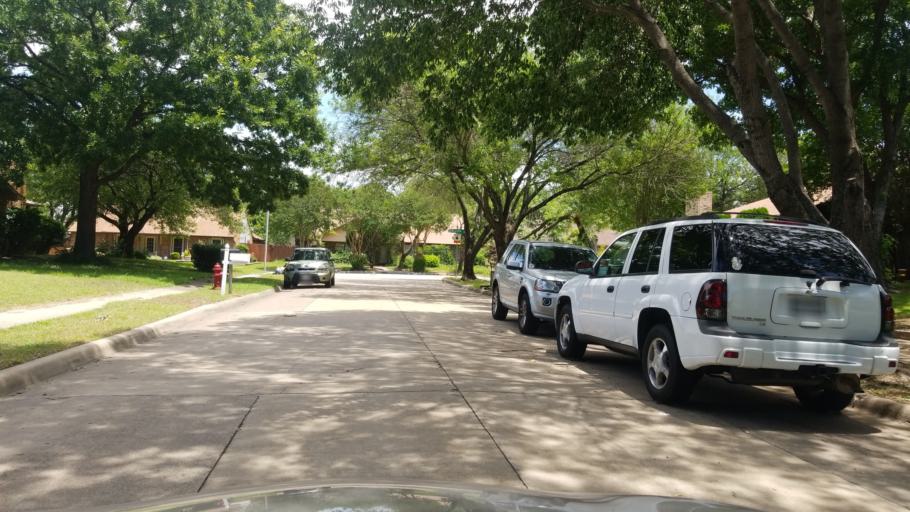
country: US
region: Texas
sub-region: Dallas County
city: Grand Prairie
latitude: 32.6826
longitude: -97.0045
